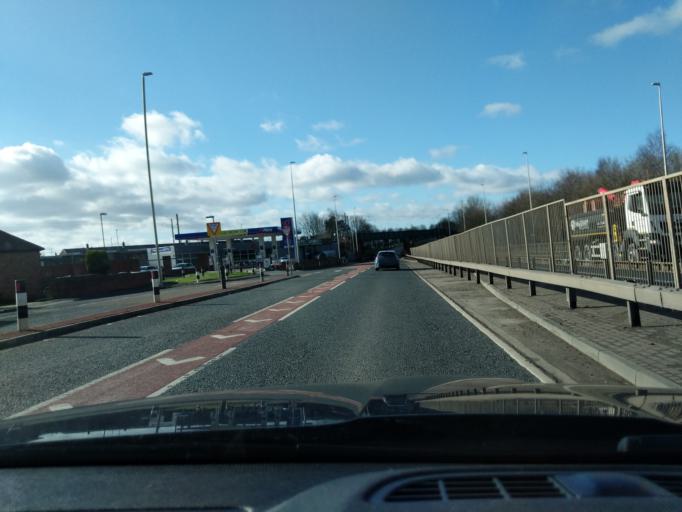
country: GB
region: England
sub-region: South Tyneside
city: Jarrow
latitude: 54.9578
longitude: -1.4928
